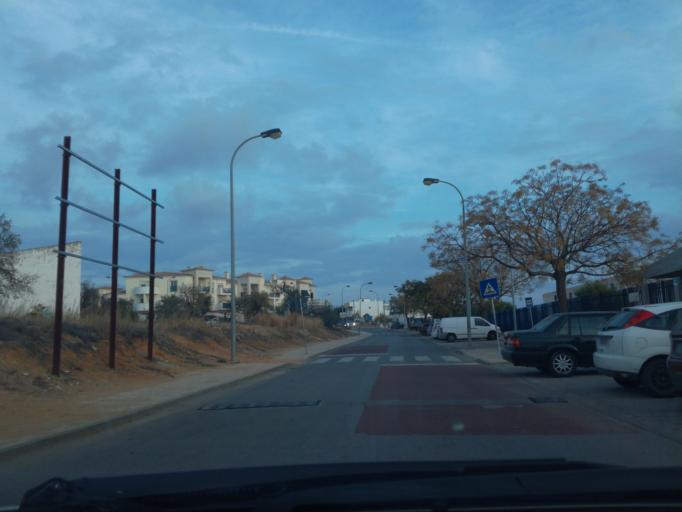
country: PT
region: Faro
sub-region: Sao Bras de Alportel
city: Sao Bras de Alportel
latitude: 37.0925
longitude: -7.8950
